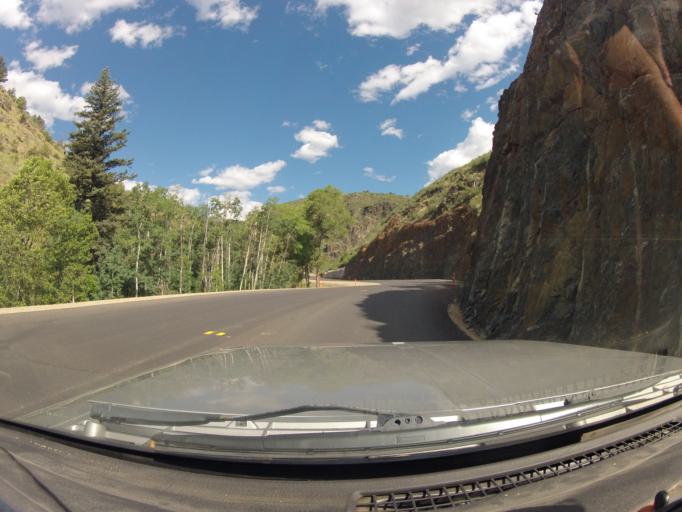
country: US
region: Colorado
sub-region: Larimer County
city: Laporte
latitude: 40.5628
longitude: -105.3031
